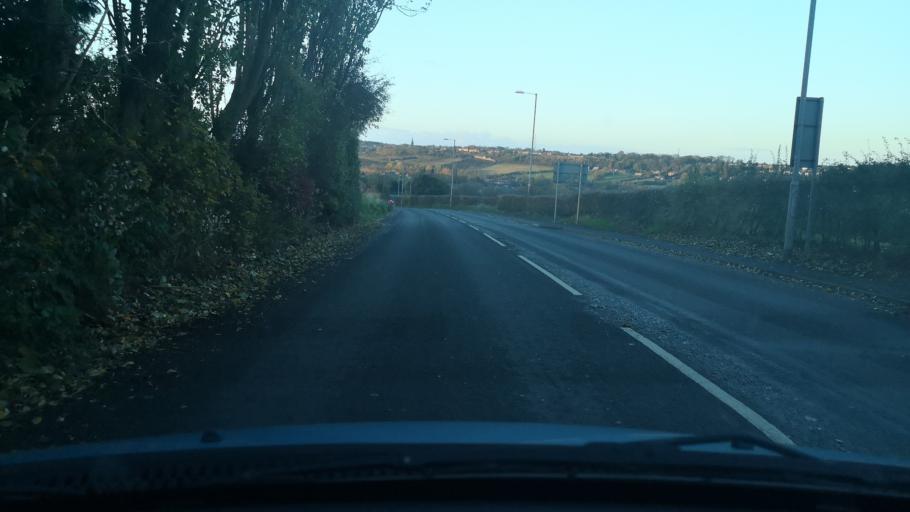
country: GB
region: England
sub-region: City and Borough of Wakefield
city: Horbury
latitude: 53.6512
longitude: -1.5741
